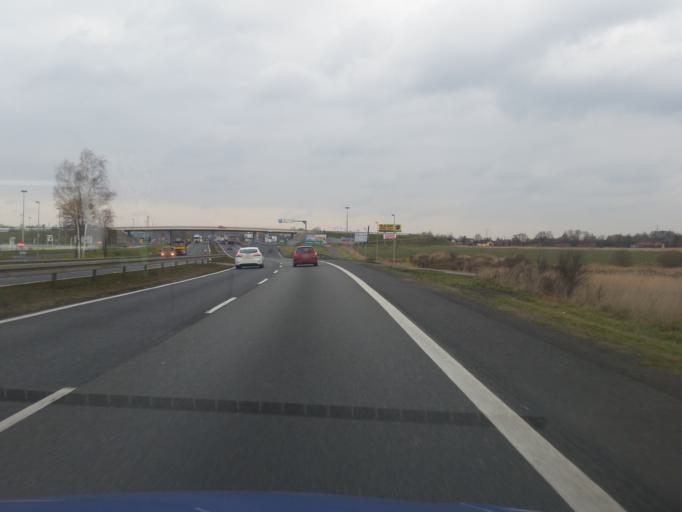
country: PL
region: Silesian Voivodeship
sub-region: Powiat czestochowski
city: Huta Stara B
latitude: 50.7267
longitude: 19.1603
